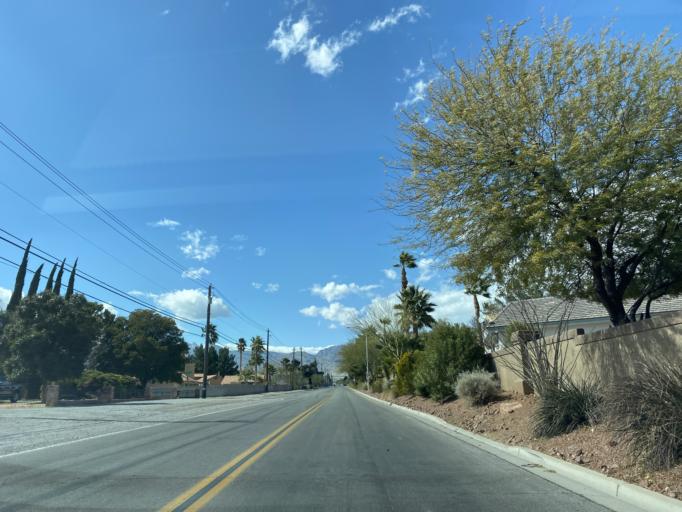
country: US
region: Nevada
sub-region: Clark County
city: Spring Valley
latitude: 36.2556
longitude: -115.2710
